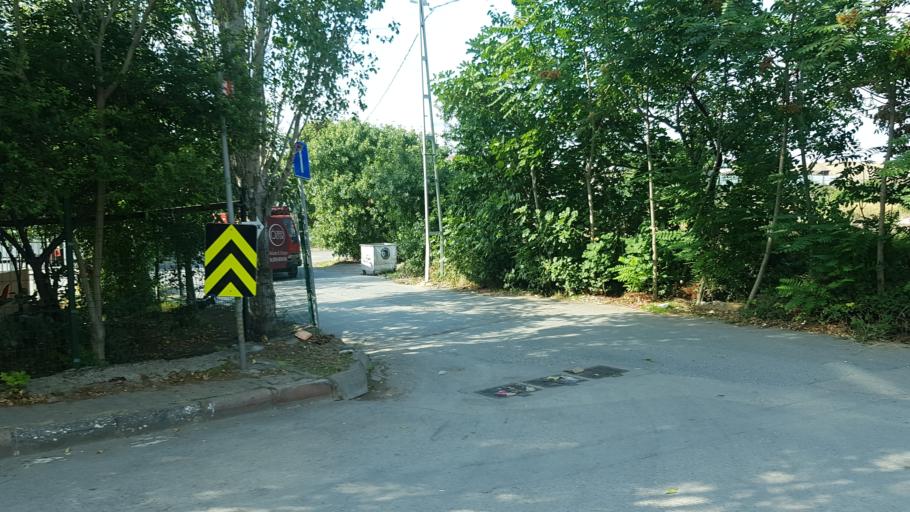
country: TR
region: Istanbul
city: Maltepe
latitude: 40.9005
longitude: 29.2005
